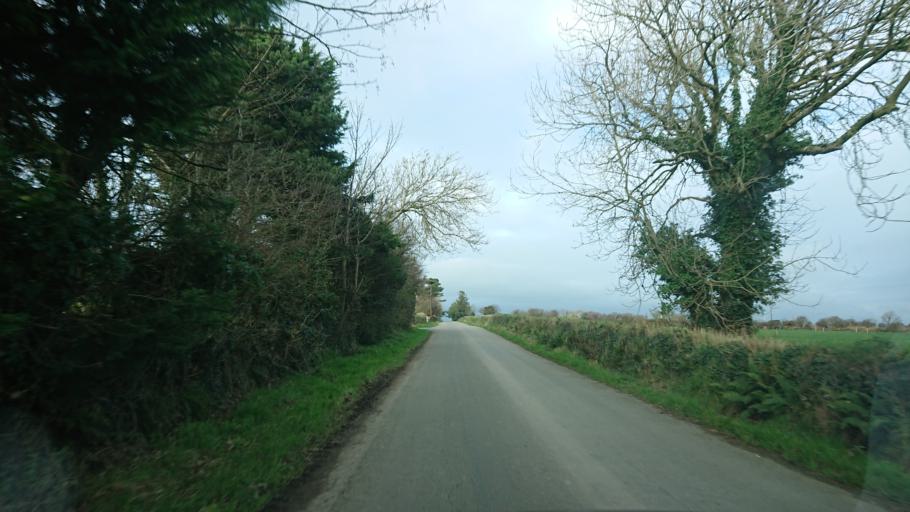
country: IE
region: Munster
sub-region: Waterford
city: Tra Mhor
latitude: 52.1474
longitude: -7.2096
